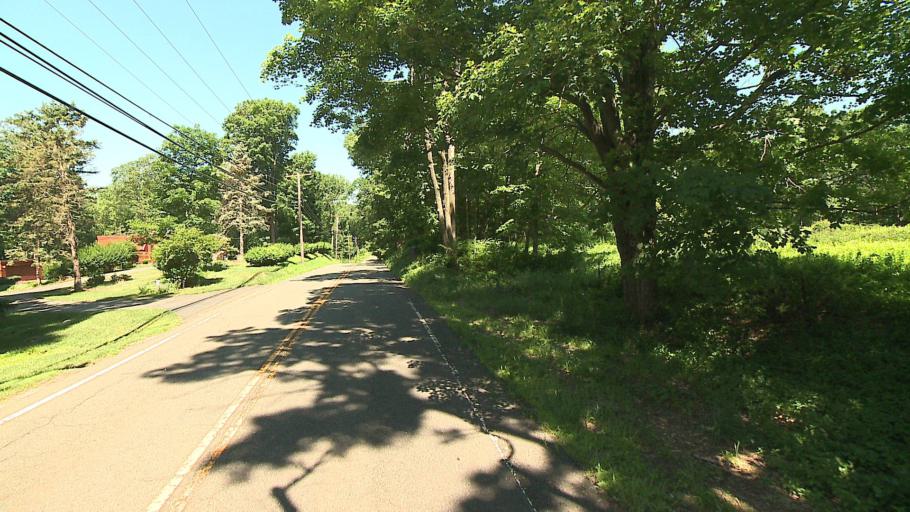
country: US
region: Connecticut
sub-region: Fairfield County
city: Ridgefield
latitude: 41.2951
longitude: -73.5313
